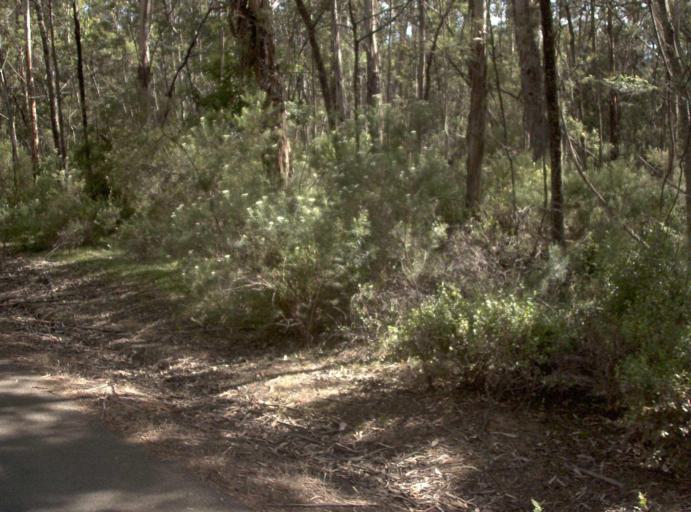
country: AU
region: Victoria
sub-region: East Gippsland
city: Lakes Entrance
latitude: -37.4340
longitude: 148.1295
